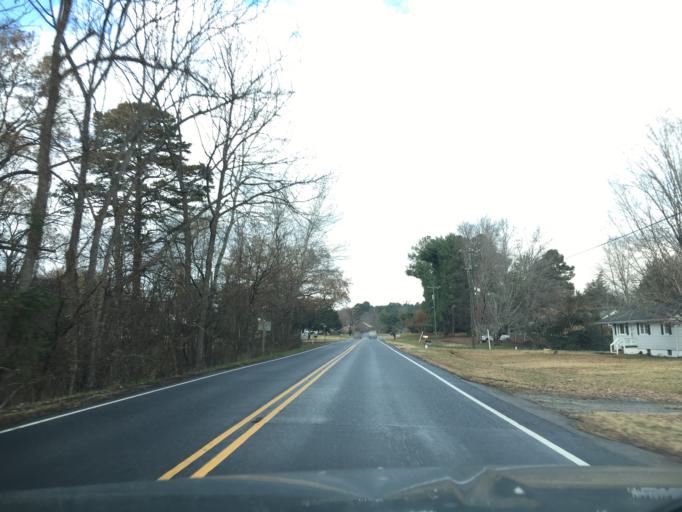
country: US
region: Virginia
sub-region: Prince Edward County
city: Farmville
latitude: 37.3237
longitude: -78.3866
